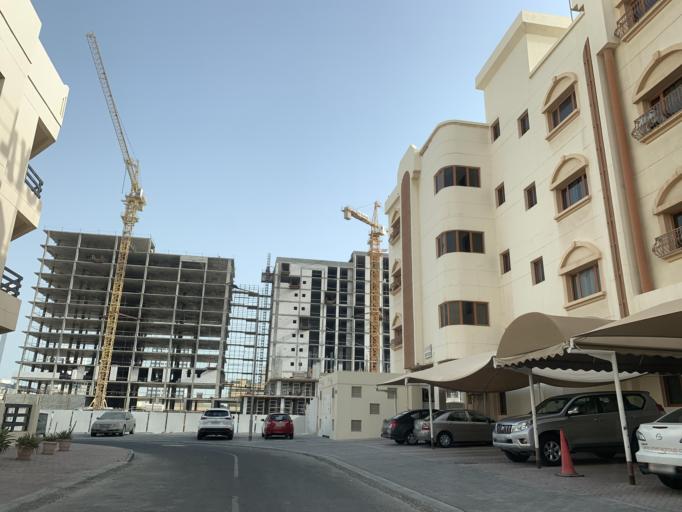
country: BH
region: Manama
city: Manama
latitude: 26.2163
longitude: 50.6147
